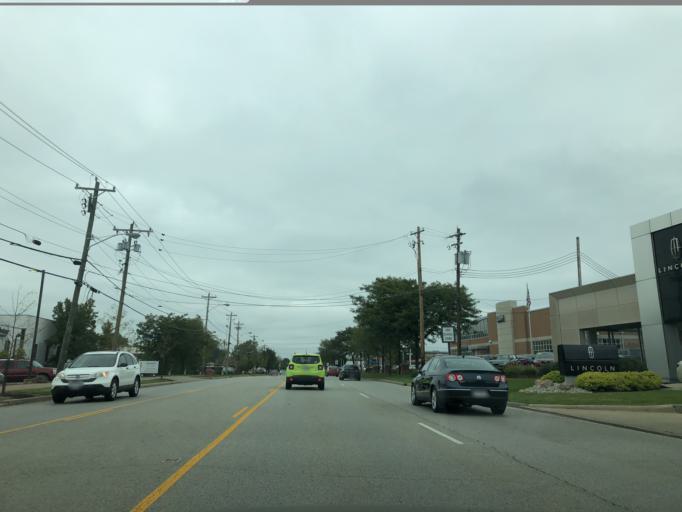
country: US
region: Ohio
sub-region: Hamilton County
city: Montgomery
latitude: 39.2310
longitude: -84.3527
